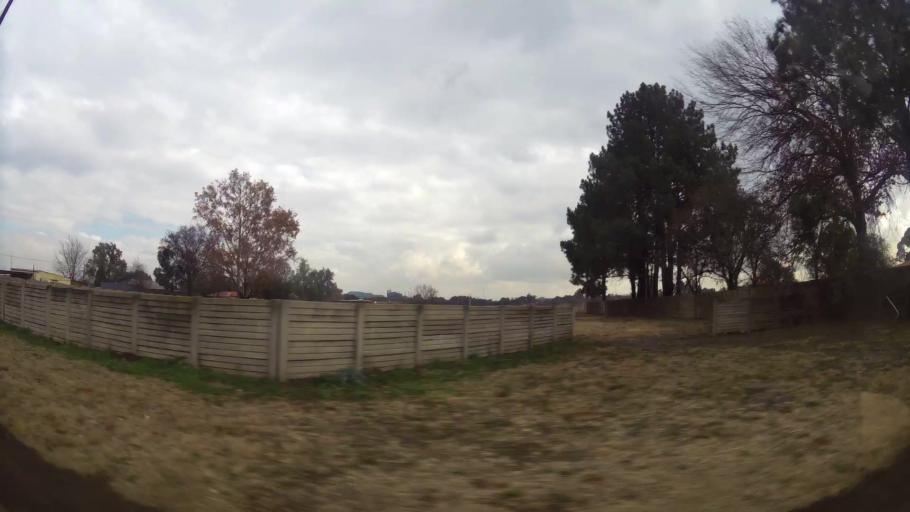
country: ZA
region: Gauteng
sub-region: Sedibeng District Municipality
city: Meyerton
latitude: -26.5824
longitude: 28.0004
